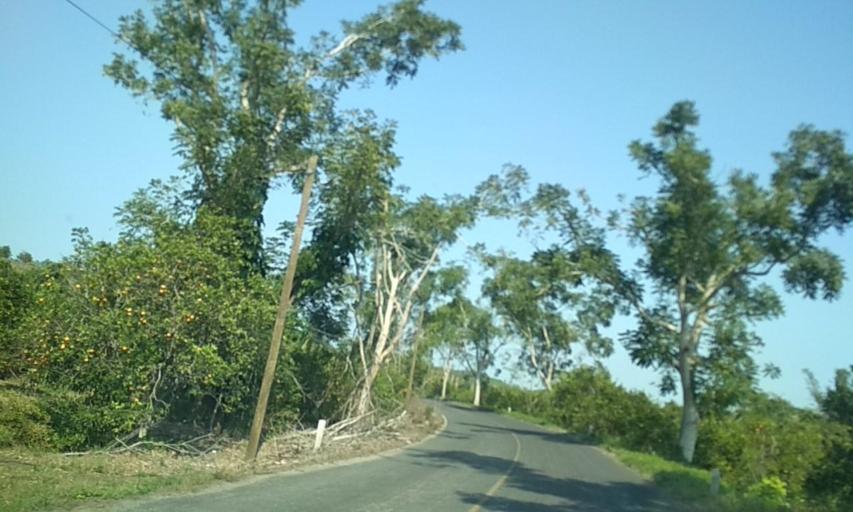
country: MX
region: Veracruz
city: Gutierrez Zamora
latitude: 20.3476
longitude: -97.1484
